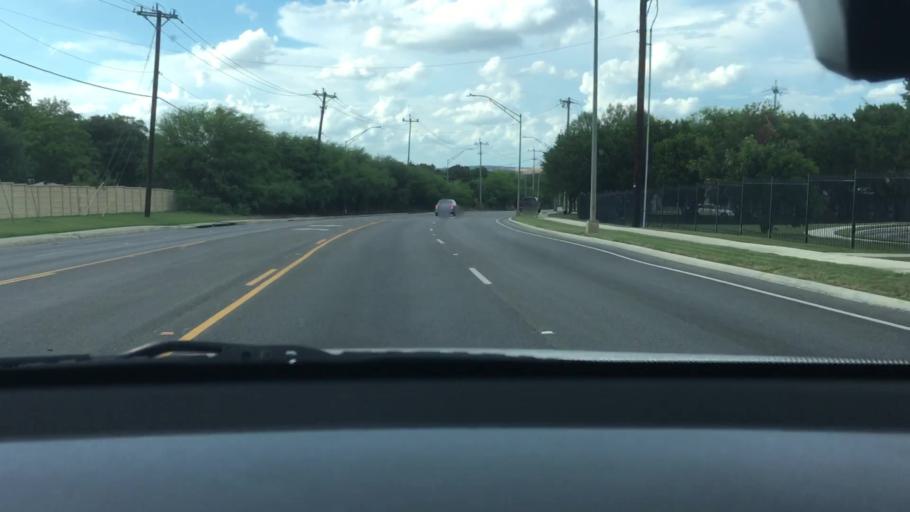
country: US
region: Texas
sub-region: Bexar County
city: Live Oak
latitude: 29.5986
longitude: -98.4043
